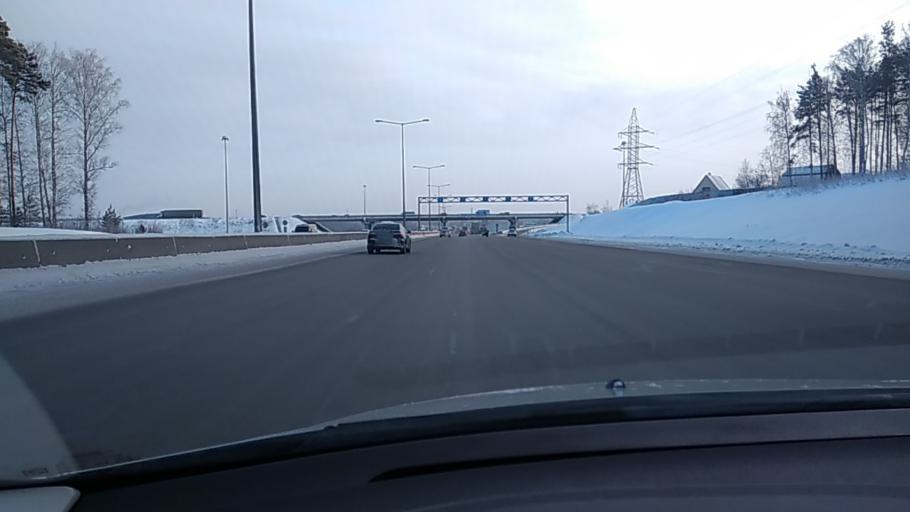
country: RU
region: Sverdlovsk
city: Istok
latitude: 56.7695
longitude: 60.7324
